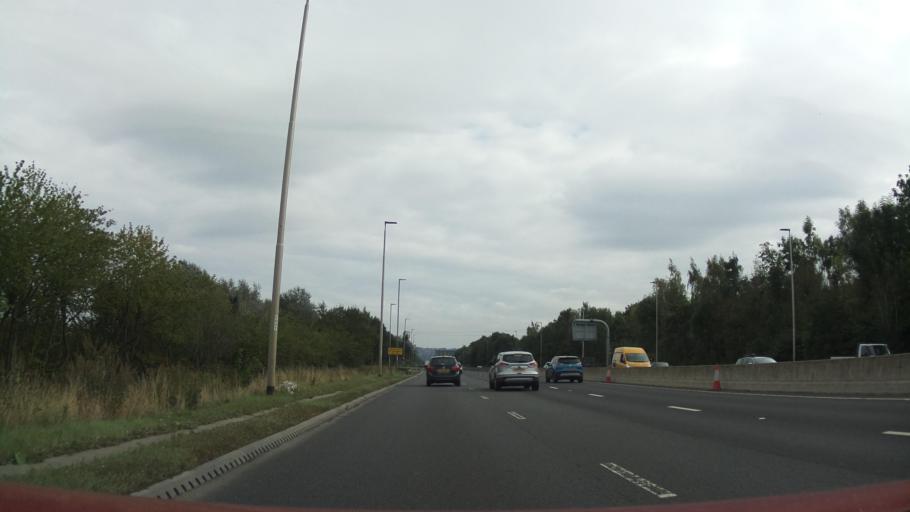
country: GB
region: England
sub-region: Gateshead
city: Whickham
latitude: 54.9532
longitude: -1.6615
